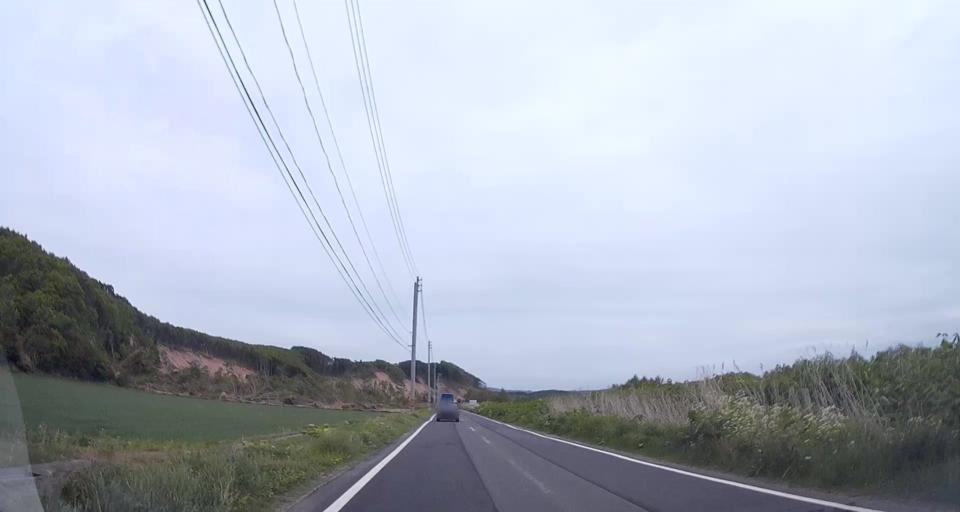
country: JP
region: Hokkaido
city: Chitose
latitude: 42.7432
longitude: 141.9058
